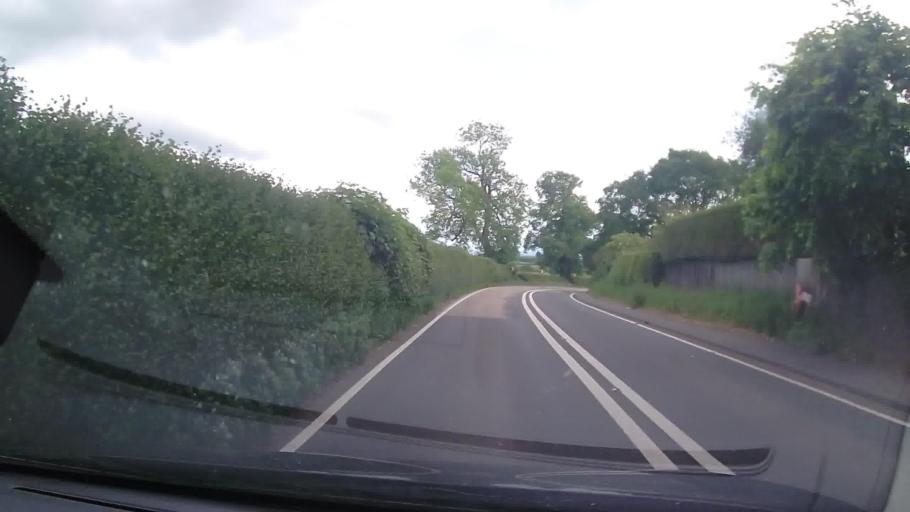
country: GB
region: England
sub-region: Shropshire
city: Astley
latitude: 52.7570
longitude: -2.7456
